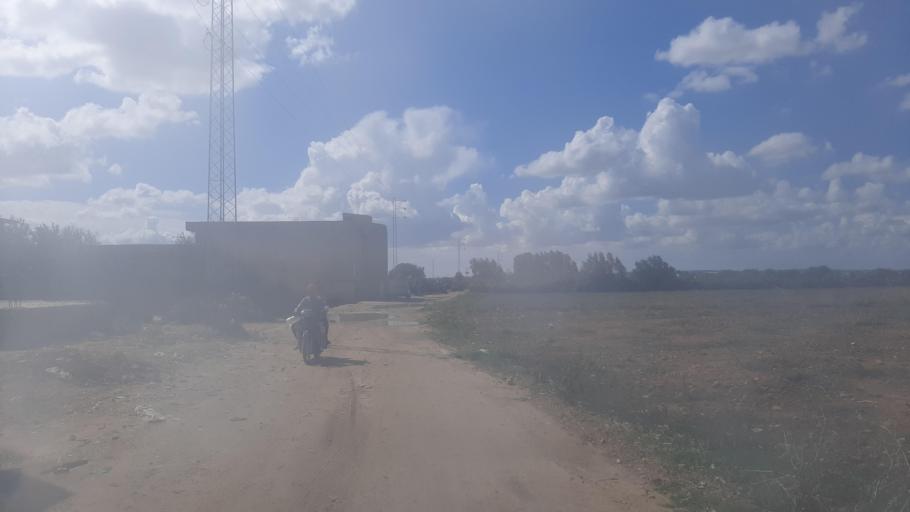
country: TN
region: Nabul
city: Korba
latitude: 36.6257
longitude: 10.8609
